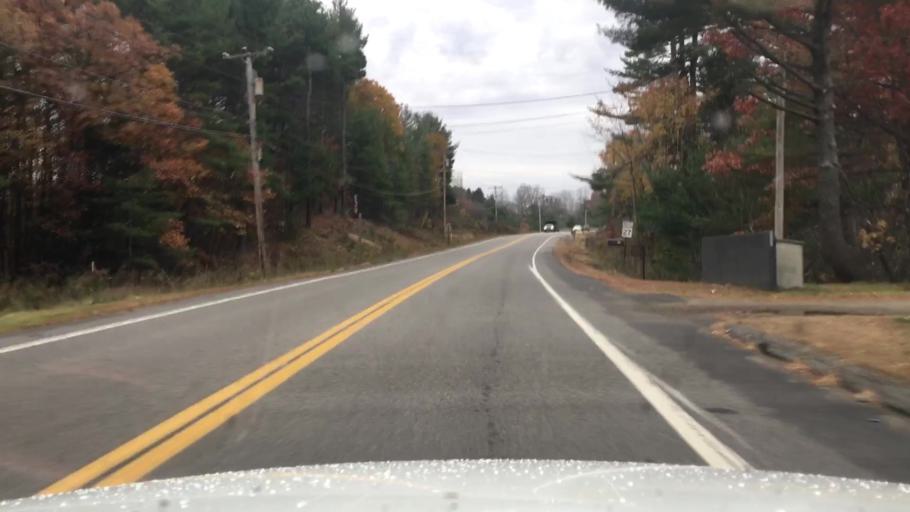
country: US
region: Maine
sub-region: Kennebec County
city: Pittston
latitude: 44.2219
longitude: -69.7573
